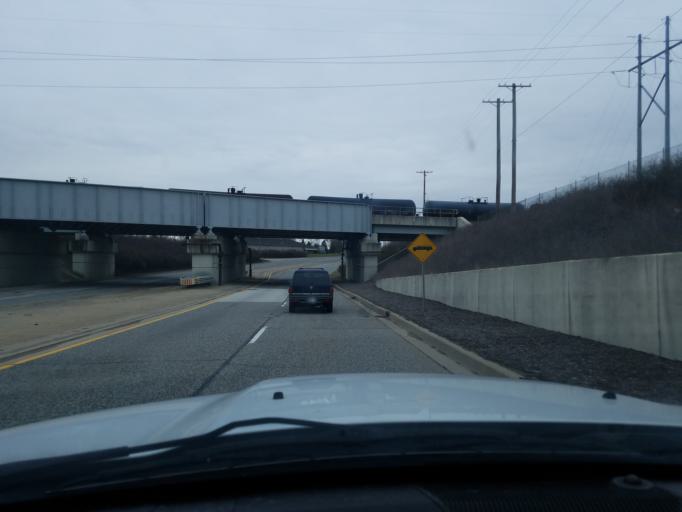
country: US
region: Indiana
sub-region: Tippecanoe County
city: Lafayette
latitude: 40.4455
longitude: -86.8649
